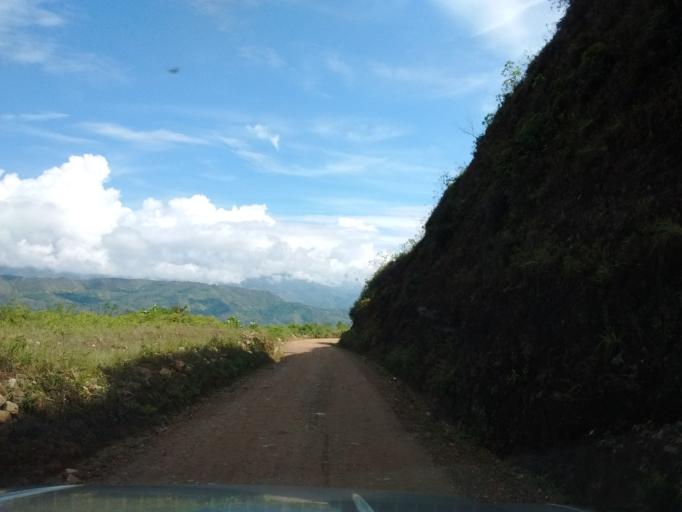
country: CO
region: Cauca
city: Morales
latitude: 2.6892
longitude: -76.7436
